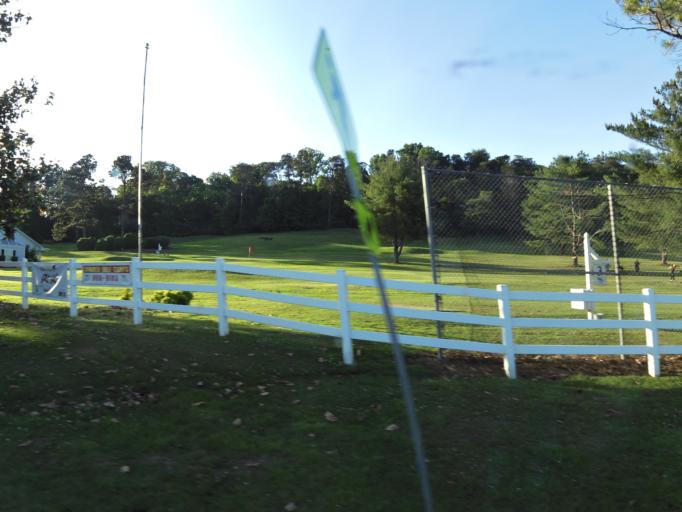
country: US
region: Tennessee
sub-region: Knox County
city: Farragut
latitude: 35.8634
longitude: -84.1246
